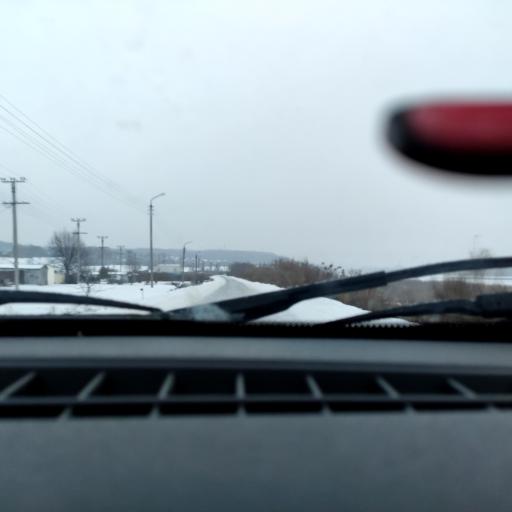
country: RU
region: Bashkortostan
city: Blagoveshchensk
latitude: 54.8948
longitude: 56.0269
